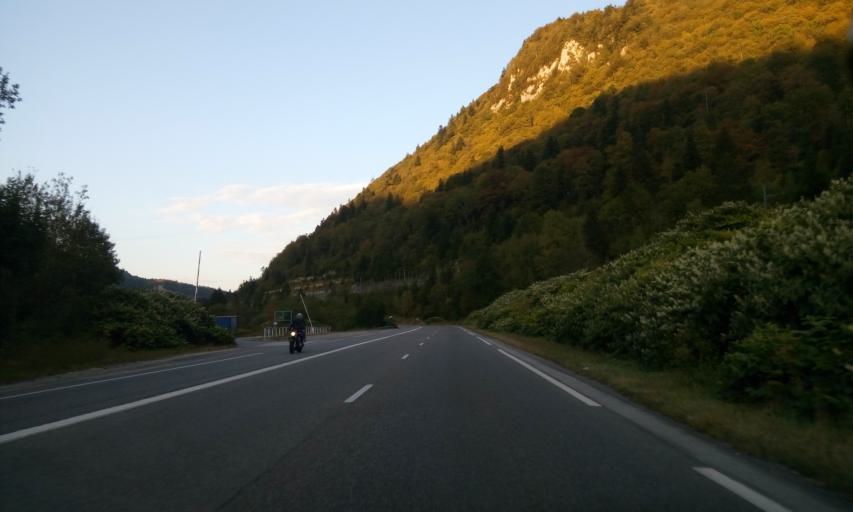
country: FR
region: Rhone-Alpes
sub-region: Departement de l'Ain
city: Nantua
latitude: 46.1444
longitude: 5.6389
